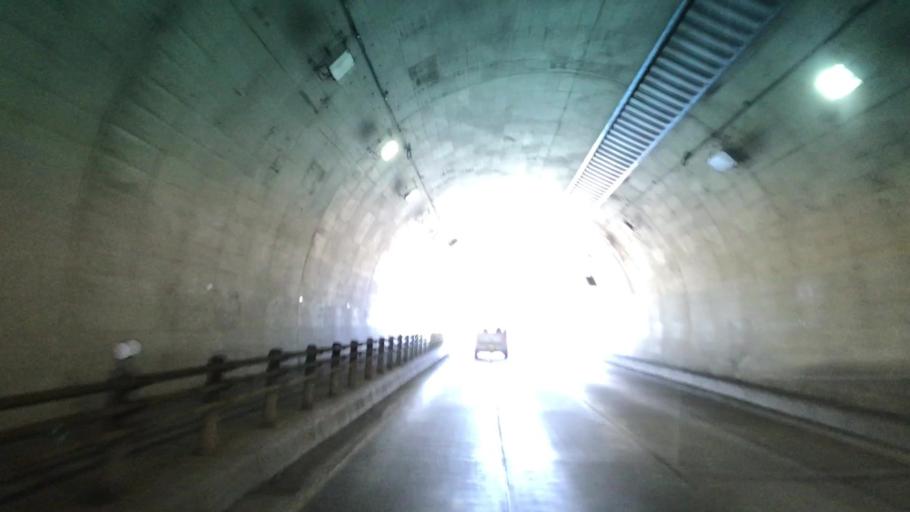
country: JP
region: Hokkaido
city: Iwanai
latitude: 43.0436
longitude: 140.5076
